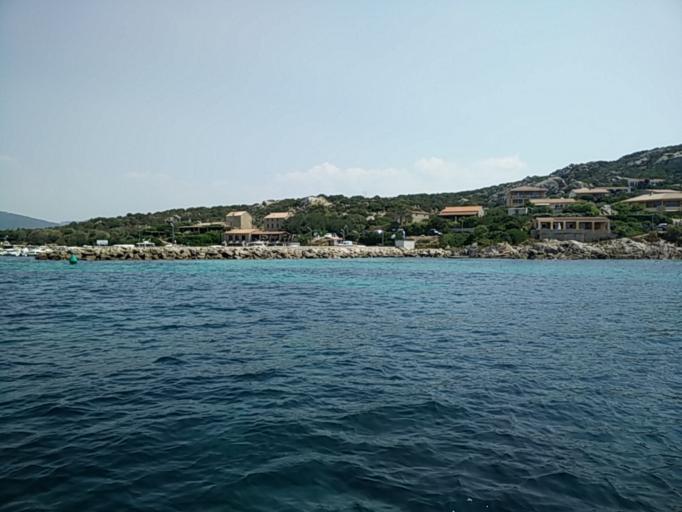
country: FR
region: Corsica
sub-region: Departement de la Corse-du-Sud
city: Propriano
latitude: 41.5415
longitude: 8.8497
